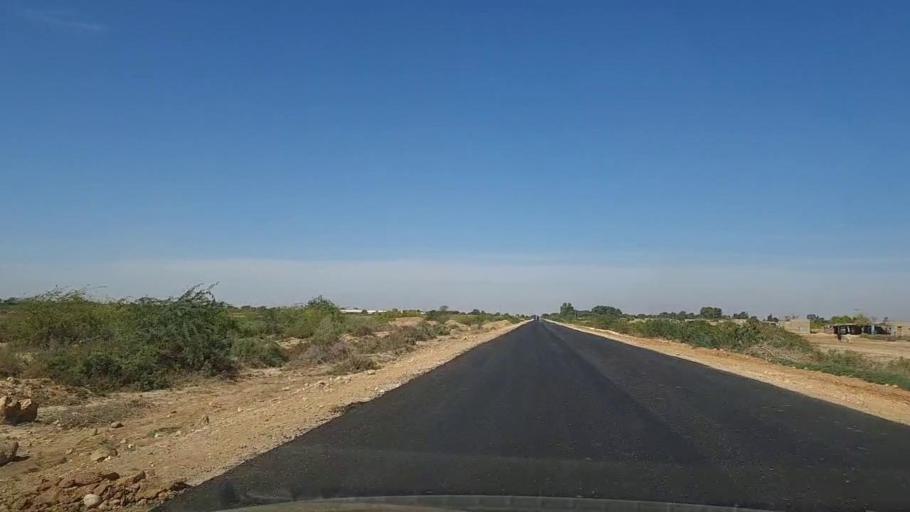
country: PK
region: Sindh
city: Kotri
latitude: 25.2250
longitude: 68.2367
